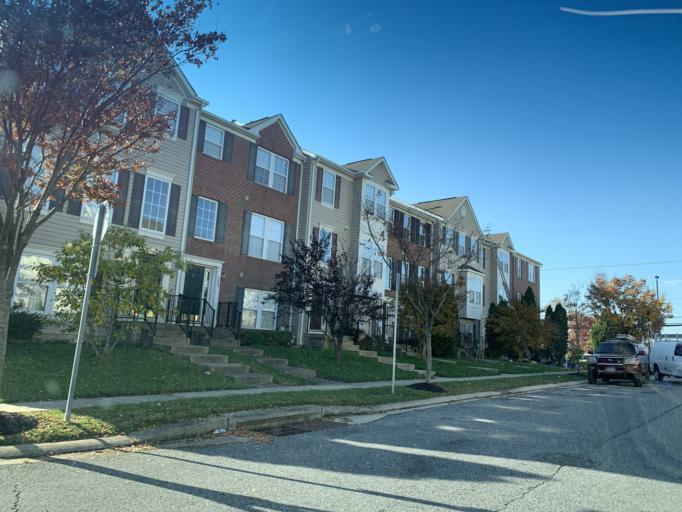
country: US
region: Maryland
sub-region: Baltimore County
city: Middle River
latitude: 39.3484
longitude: -76.4487
